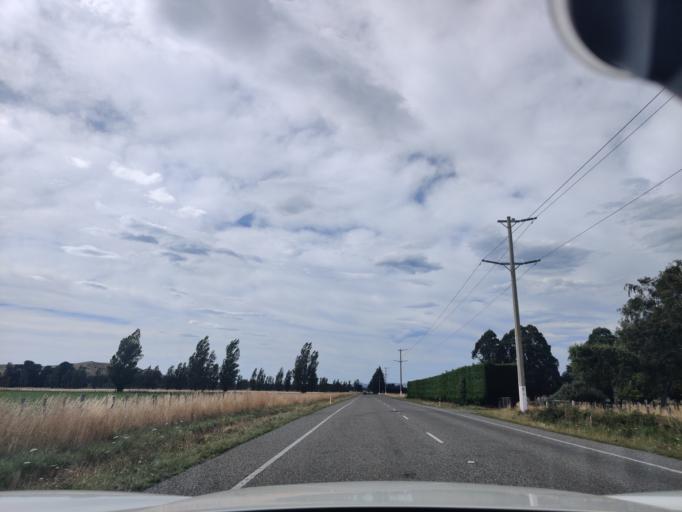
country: NZ
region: Wellington
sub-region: Masterton District
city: Masterton
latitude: -40.8493
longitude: 175.6353
